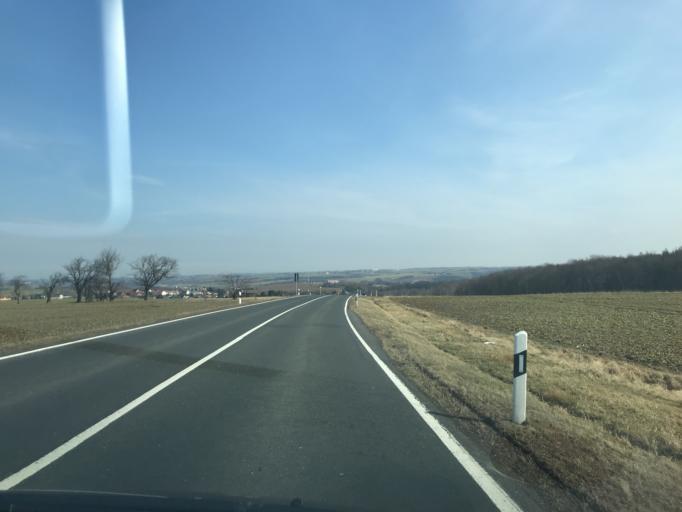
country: DE
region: Saxony
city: Wechselburg
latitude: 51.0306
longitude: 12.7566
